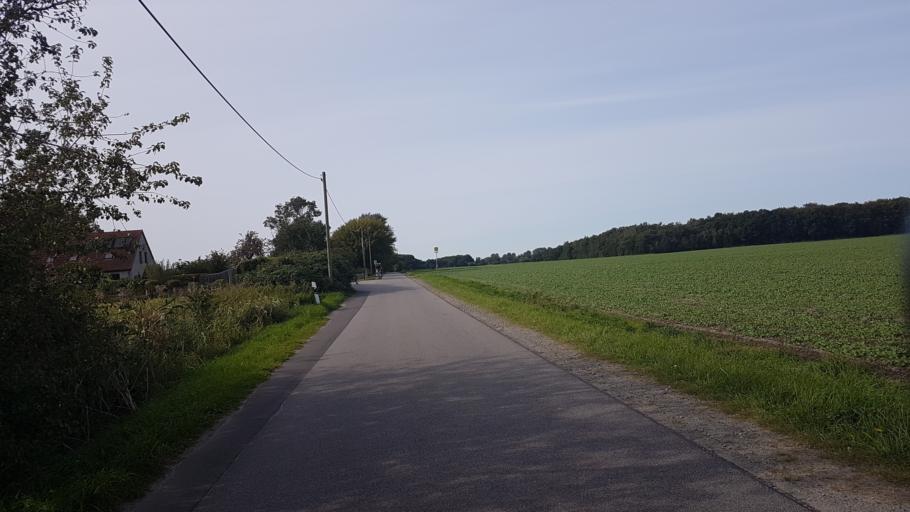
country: DE
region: Mecklenburg-Vorpommern
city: Gingst
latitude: 54.4529
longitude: 13.1449
